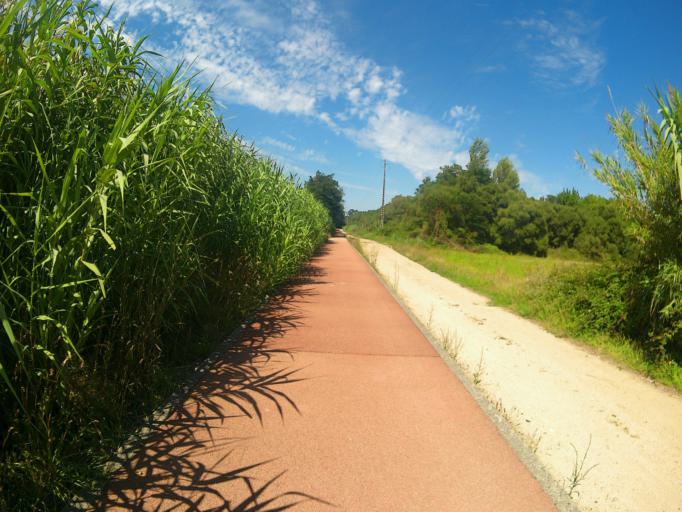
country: PT
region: Viana do Castelo
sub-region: Valenca
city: Valenca
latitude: 42.0061
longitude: -8.6560
